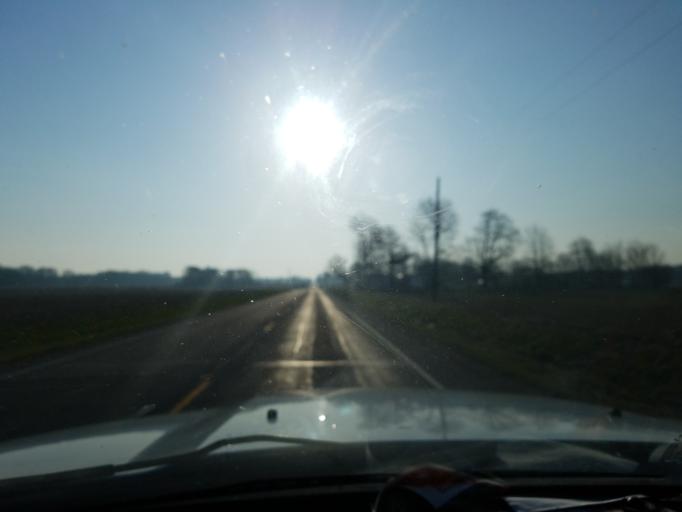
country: US
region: Indiana
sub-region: Vigo County
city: Seelyville
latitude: 39.3888
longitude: -87.1920
